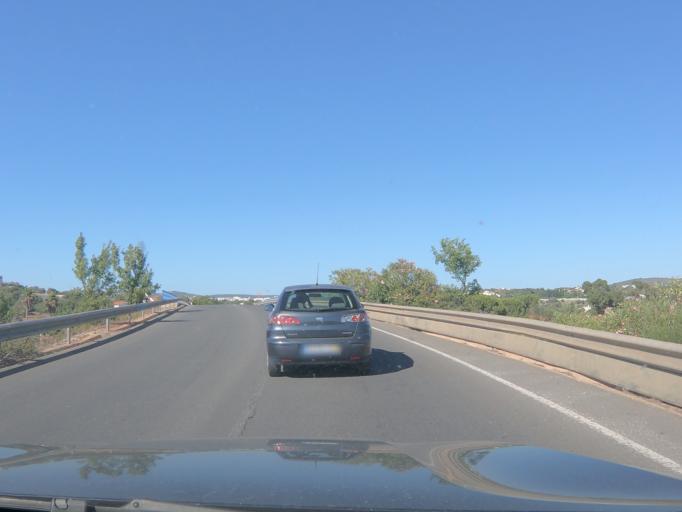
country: PT
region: Faro
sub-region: Loule
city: Almancil
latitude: 37.1029
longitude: -8.0545
